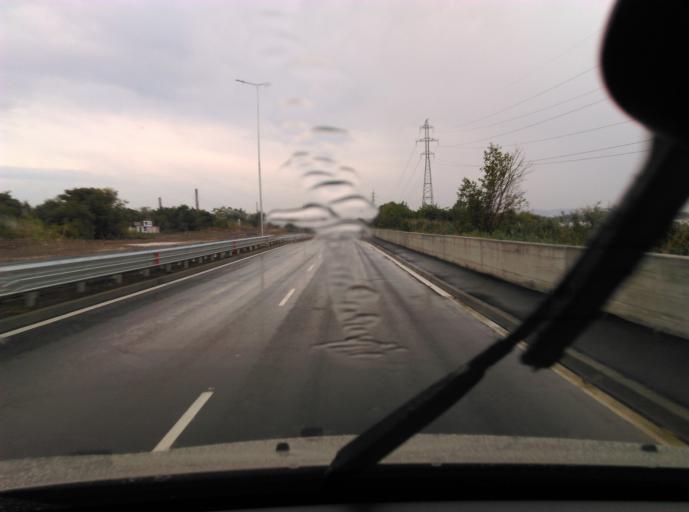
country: BG
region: Burgas
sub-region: Obshtina Burgas
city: Burgas
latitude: 42.5067
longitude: 27.4459
